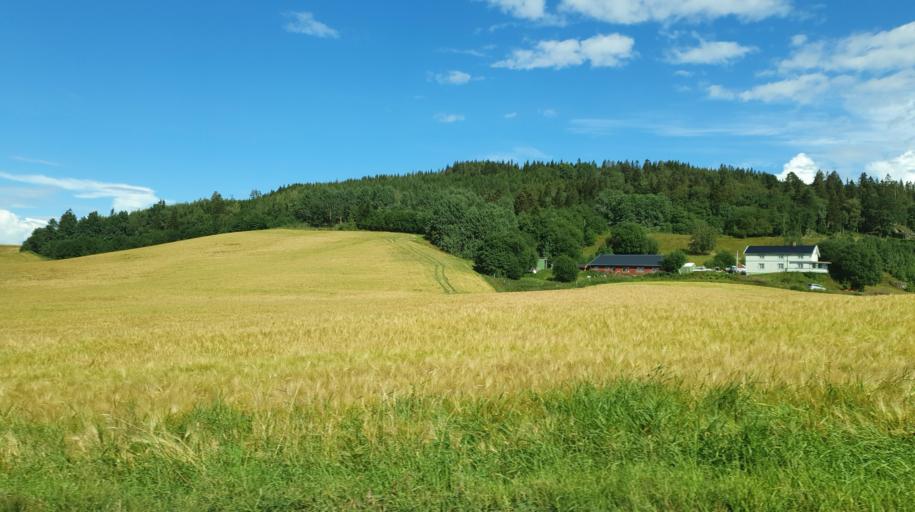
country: NO
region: Nord-Trondelag
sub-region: Levanger
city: Skogn
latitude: 63.6994
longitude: 11.2466
